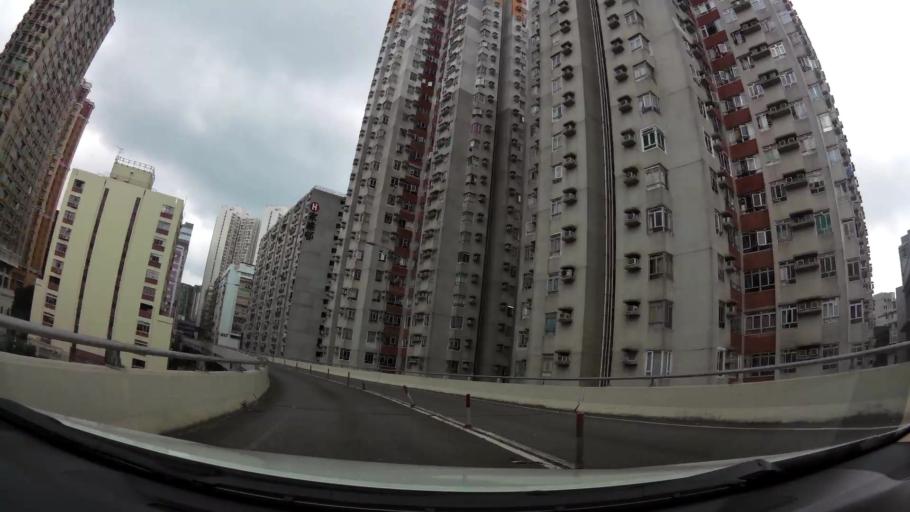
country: HK
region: Kowloon City
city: Kowloon
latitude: 22.3090
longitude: 114.1861
